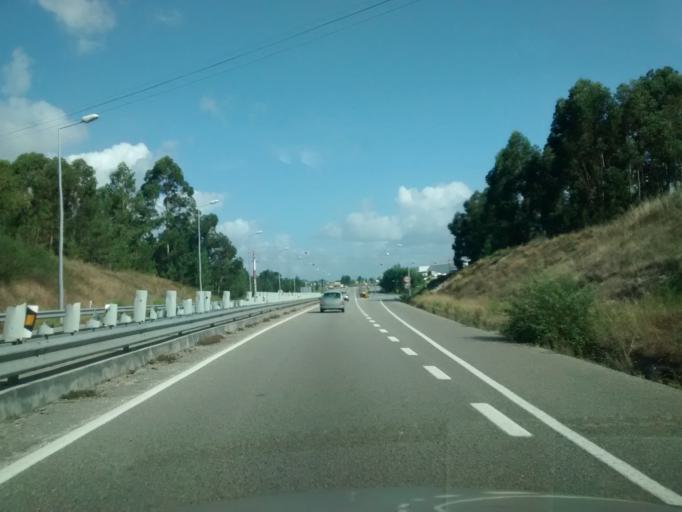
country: PT
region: Aveiro
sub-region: Oliveira do Bairro
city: Oliveira do Bairro
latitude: 40.5198
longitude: -8.5044
